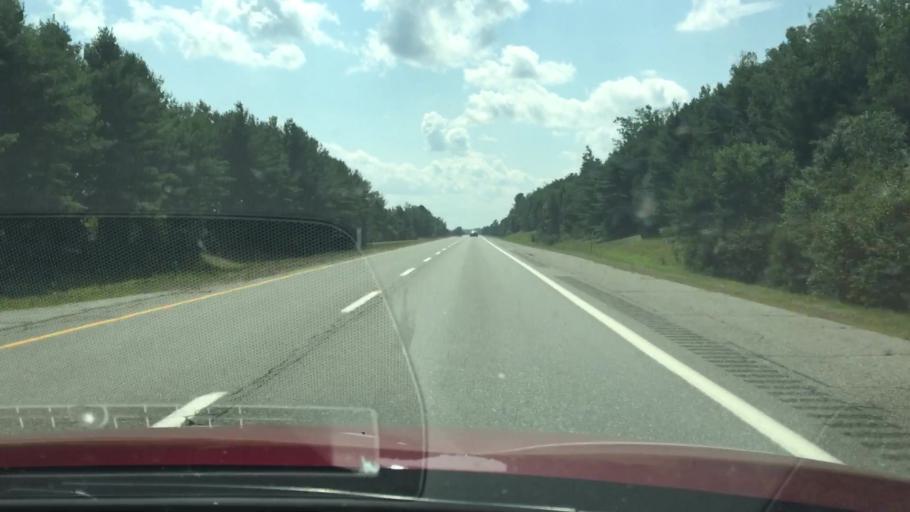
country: US
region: Maine
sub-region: Penobscot County
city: Medway
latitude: 45.4990
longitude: -68.5602
